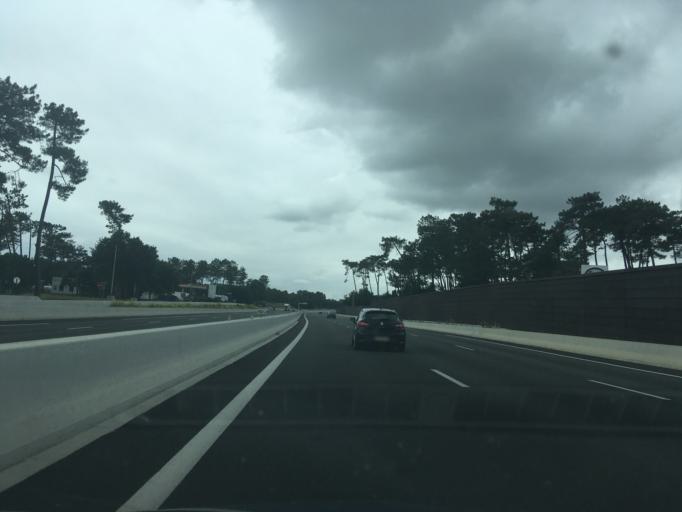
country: FR
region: Aquitaine
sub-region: Departement des Landes
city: Labenne
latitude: 43.5874
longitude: -1.4198
